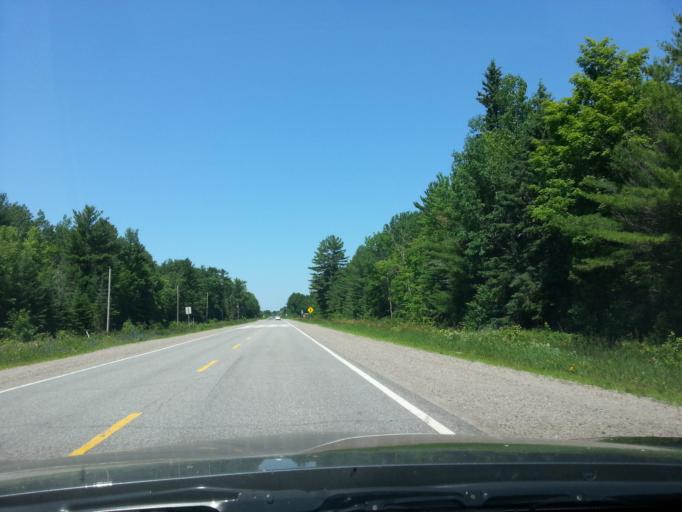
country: CA
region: Ontario
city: Arnprior
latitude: 45.5323
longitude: -76.3123
